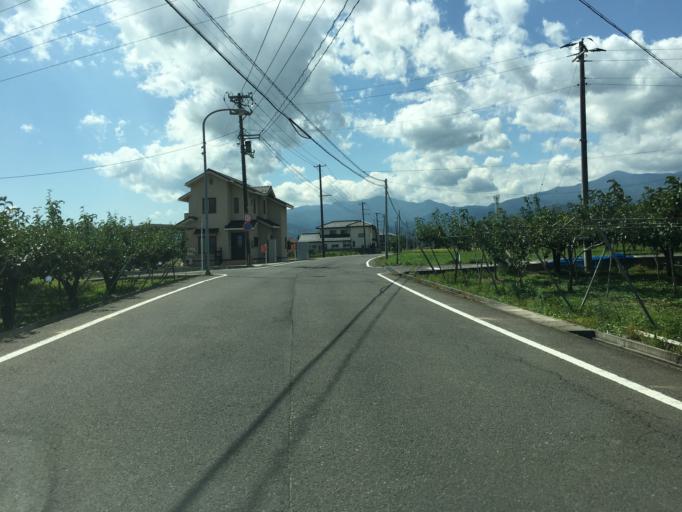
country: JP
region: Fukushima
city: Fukushima-shi
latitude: 37.7615
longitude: 140.4156
